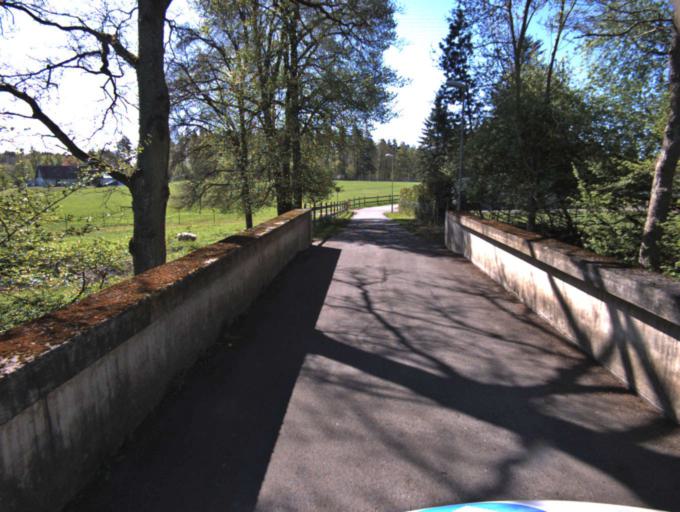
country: SE
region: Skane
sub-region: Kristianstads Kommun
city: Onnestad
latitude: 55.9285
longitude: 13.9853
